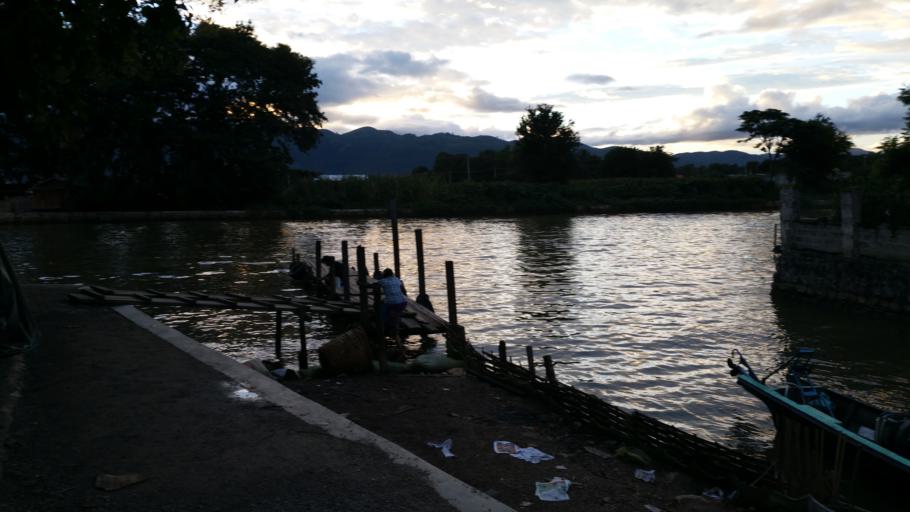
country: MM
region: Shan
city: Taunggyi
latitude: 20.6548
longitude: 96.9247
